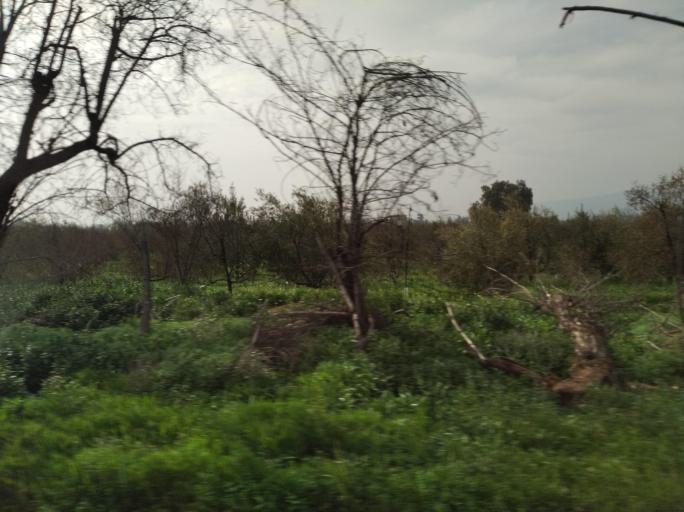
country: CL
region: Santiago Metropolitan
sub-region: Provincia de Chacabuco
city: Lampa
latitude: -33.1652
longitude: -70.8940
